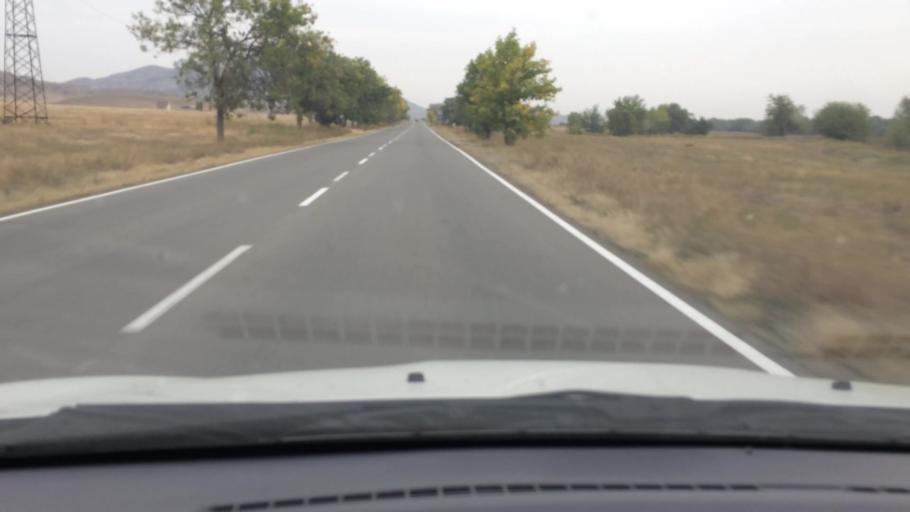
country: GE
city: Naghvarevi
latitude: 41.3334
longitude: 44.8065
